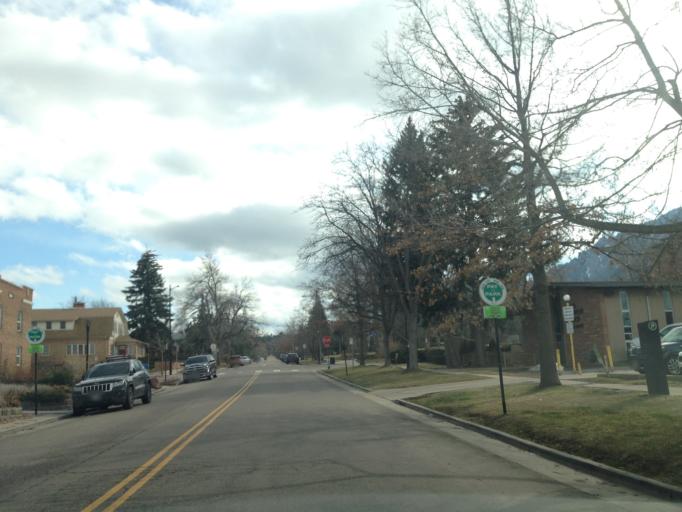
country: US
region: Colorado
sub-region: Boulder County
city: Boulder
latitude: 40.0062
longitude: -105.2762
